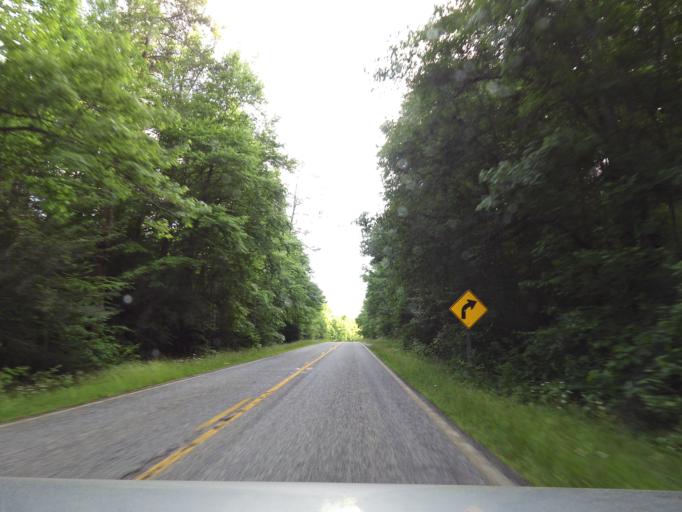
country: US
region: Georgia
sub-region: Towns County
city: Hiawassee
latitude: 34.8260
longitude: -83.8137
